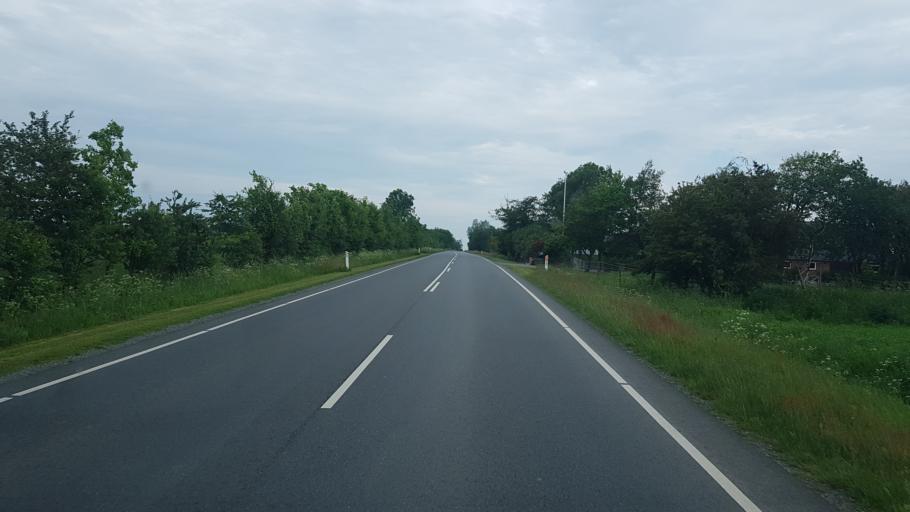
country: DK
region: South Denmark
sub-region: Vejen Kommune
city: Brorup
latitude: 55.4189
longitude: 9.0237
